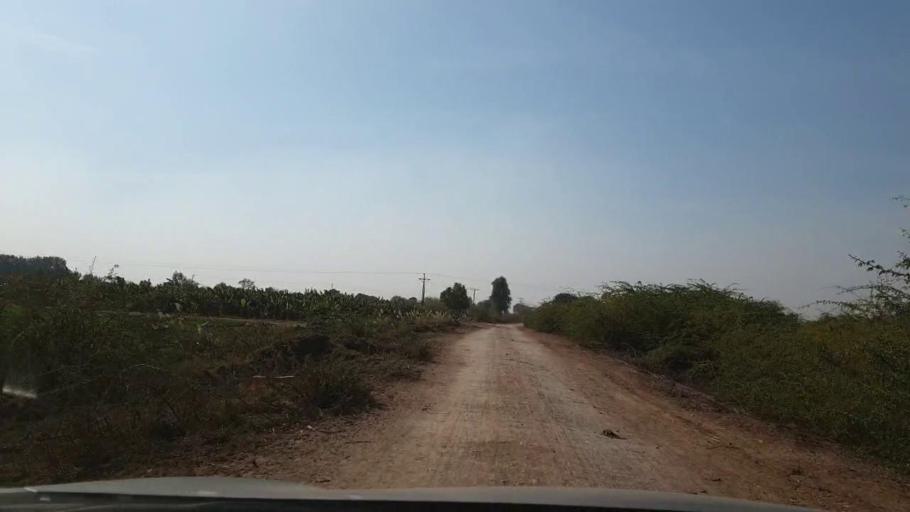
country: PK
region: Sindh
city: Berani
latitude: 25.7156
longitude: 68.7772
